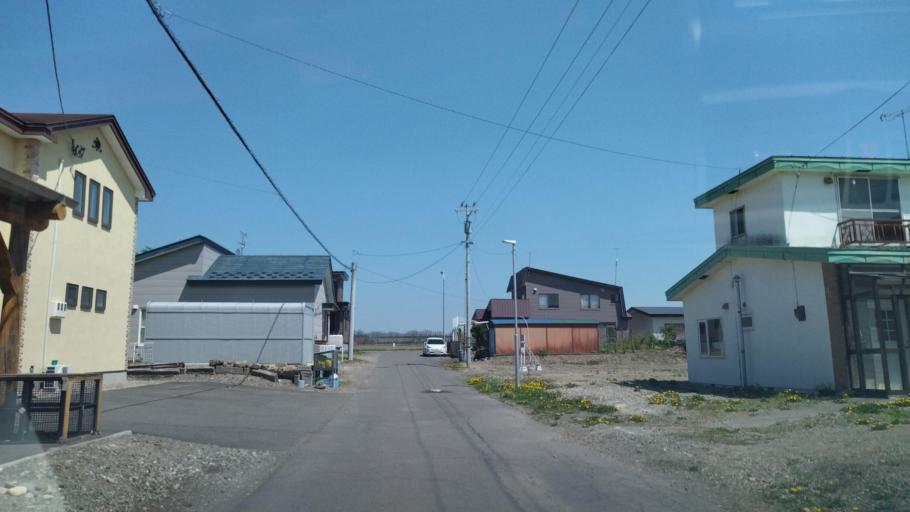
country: JP
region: Hokkaido
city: Otofuke
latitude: 43.2399
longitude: 143.2907
